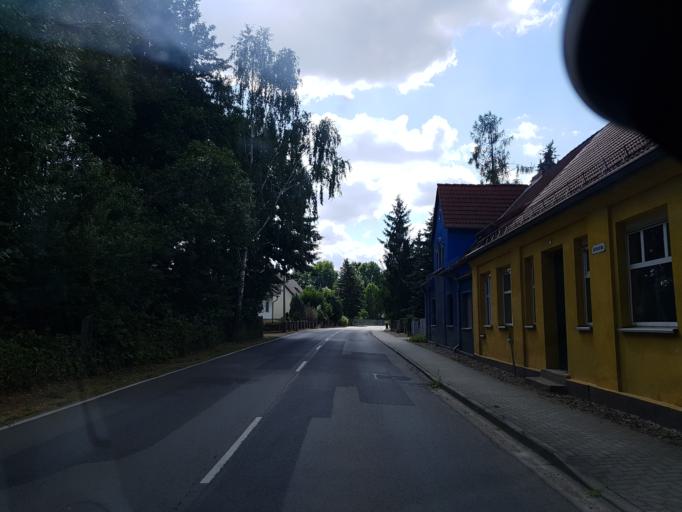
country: DE
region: Brandenburg
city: Drebkau
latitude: 51.6582
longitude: 14.2166
